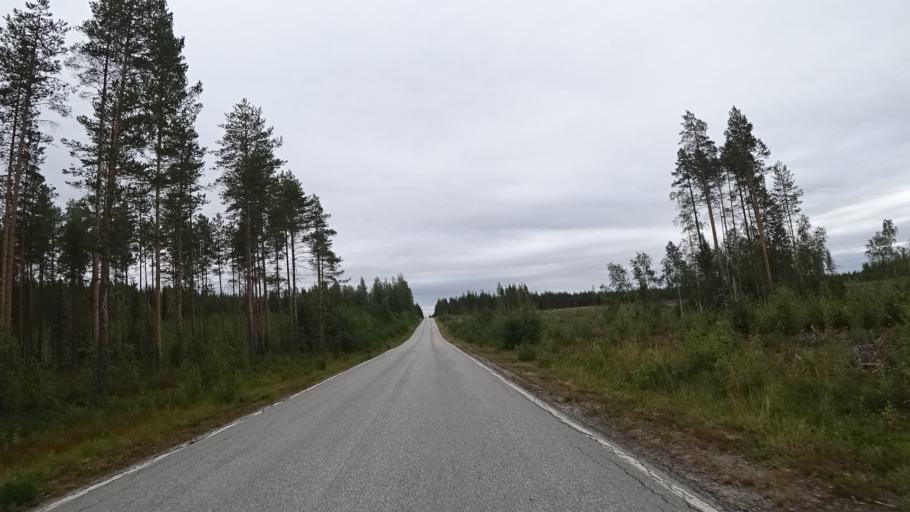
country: FI
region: North Karelia
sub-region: Pielisen Karjala
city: Lieksa
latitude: 63.3607
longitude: 30.2700
